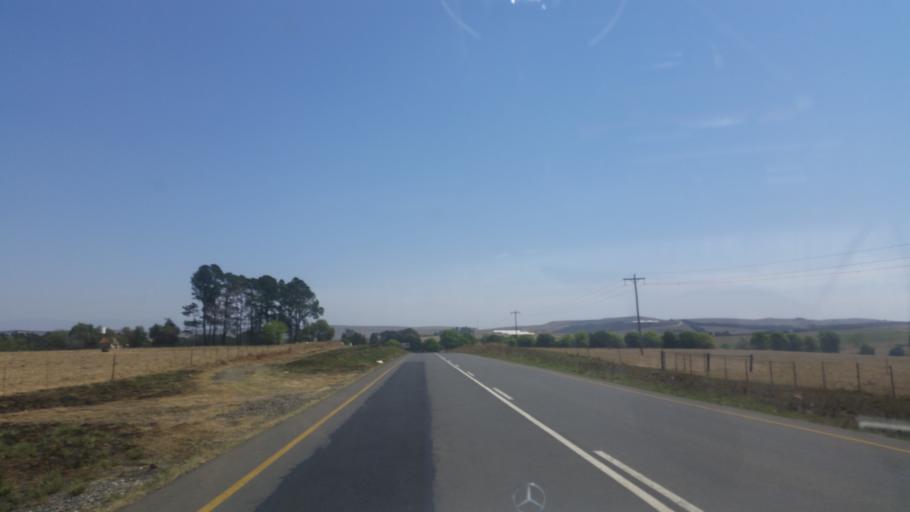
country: ZA
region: KwaZulu-Natal
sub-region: uMgungundlovu District Municipality
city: Mooirivier
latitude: -29.1492
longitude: 29.9810
